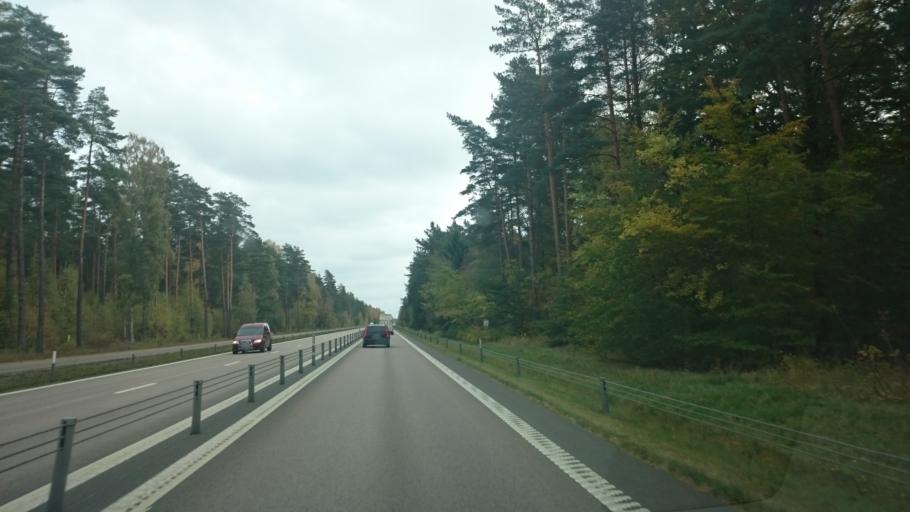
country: SE
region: Skane
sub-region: Sjobo Kommun
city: Blentarp
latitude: 55.6398
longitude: 13.6207
